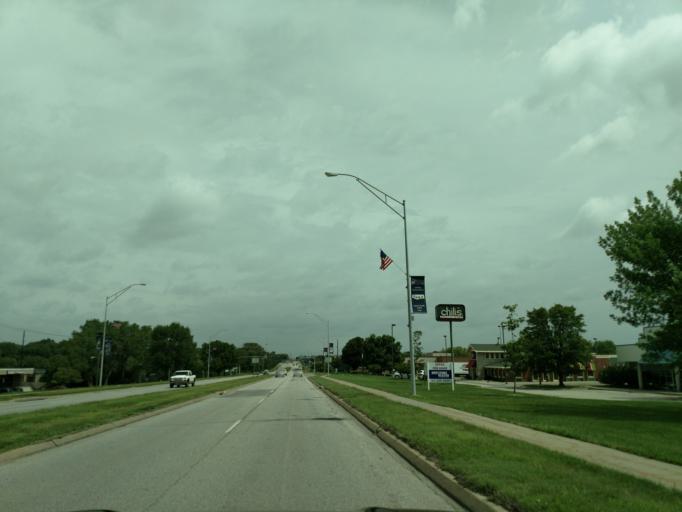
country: US
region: Nebraska
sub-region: Sarpy County
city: La Vista
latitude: 41.1815
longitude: -96.0429
